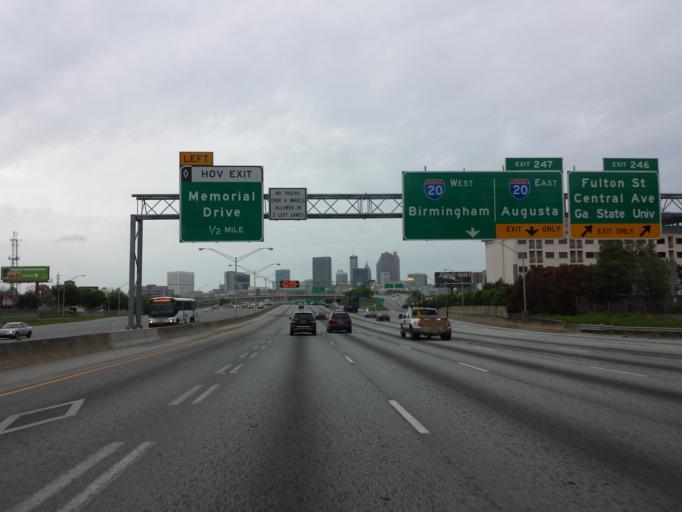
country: US
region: Georgia
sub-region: Fulton County
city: Atlanta
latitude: 33.7329
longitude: -84.3920
